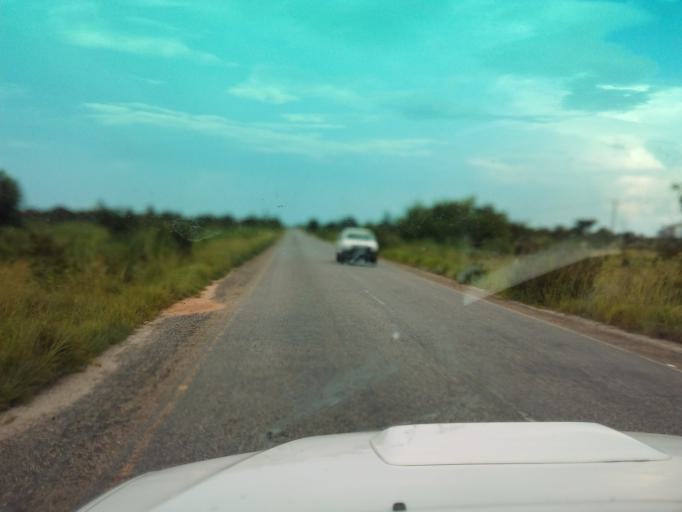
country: MZ
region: Zambezia
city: Quelimane
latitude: -17.4987
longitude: 36.9222
